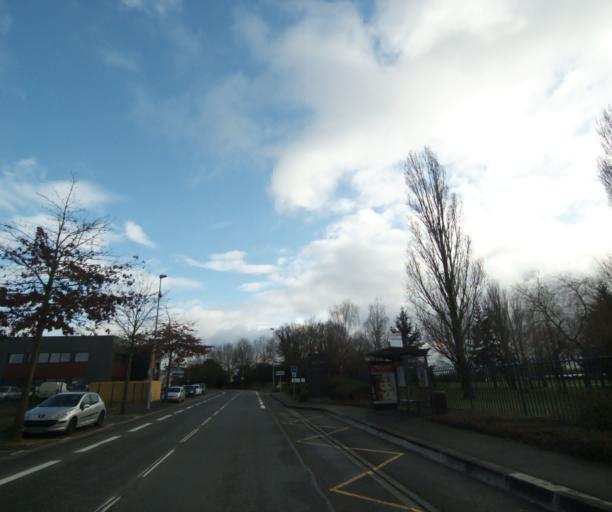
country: FR
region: Pays de la Loire
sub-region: Departement de la Sarthe
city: Rouillon
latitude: 48.0120
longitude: 0.1530
